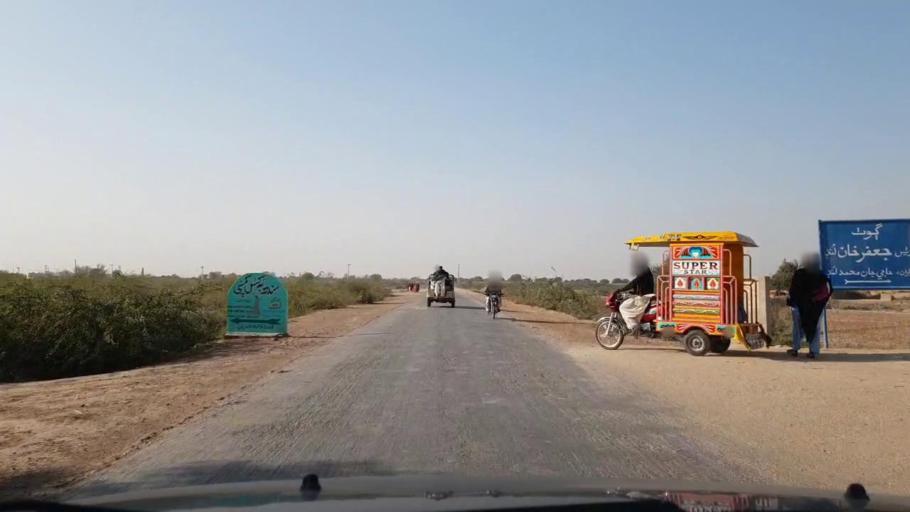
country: PK
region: Sindh
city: Tando Ghulam Ali
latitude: 25.1425
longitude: 68.8700
